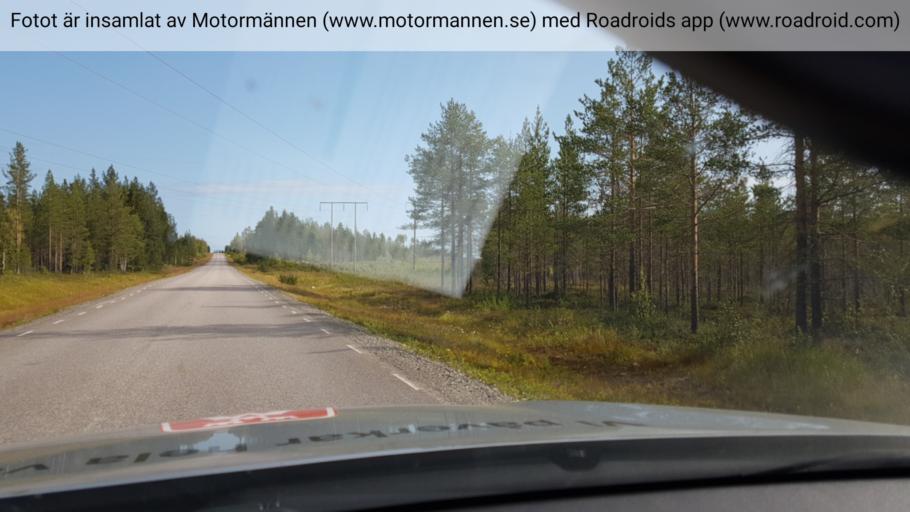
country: SE
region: Vaesterbotten
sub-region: Skelleftea Kommun
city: Storvik
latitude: 65.5361
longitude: 20.5952
